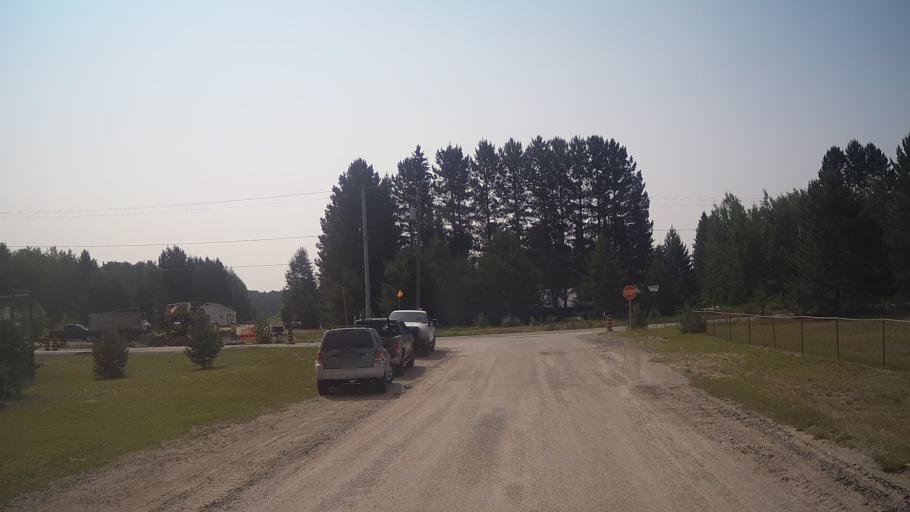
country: CA
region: Ontario
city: Timmins
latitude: 47.6774
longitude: -81.7186
